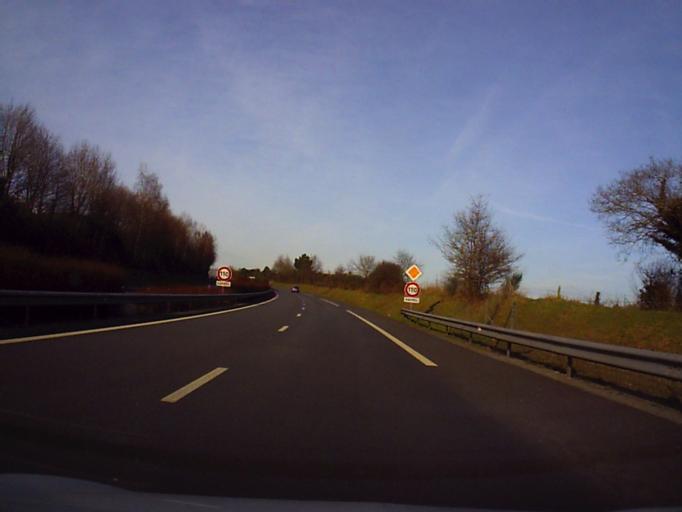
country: FR
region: Brittany
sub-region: Departement du Morbihan
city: Trefflean
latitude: 47.7012
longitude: -2.6201
